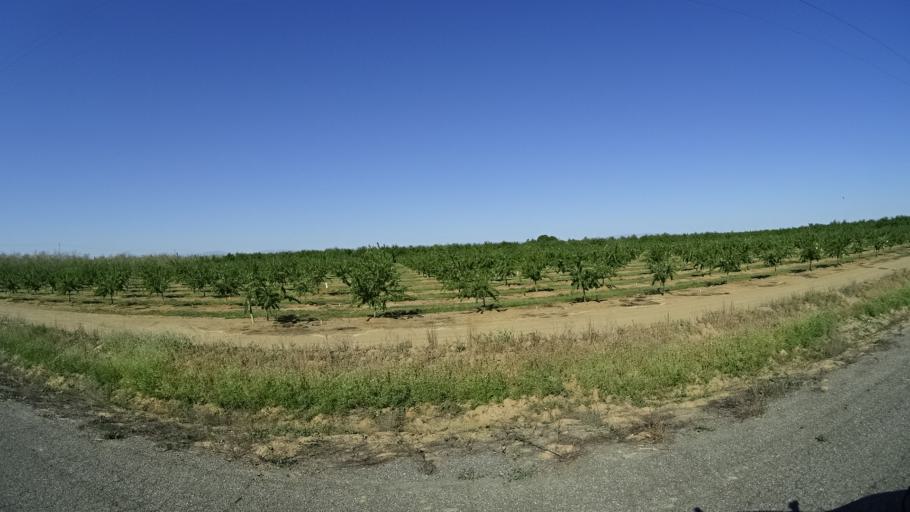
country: US
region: California
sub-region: Glenn County
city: Hamilton City
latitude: 39.6972
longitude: -122.0742
